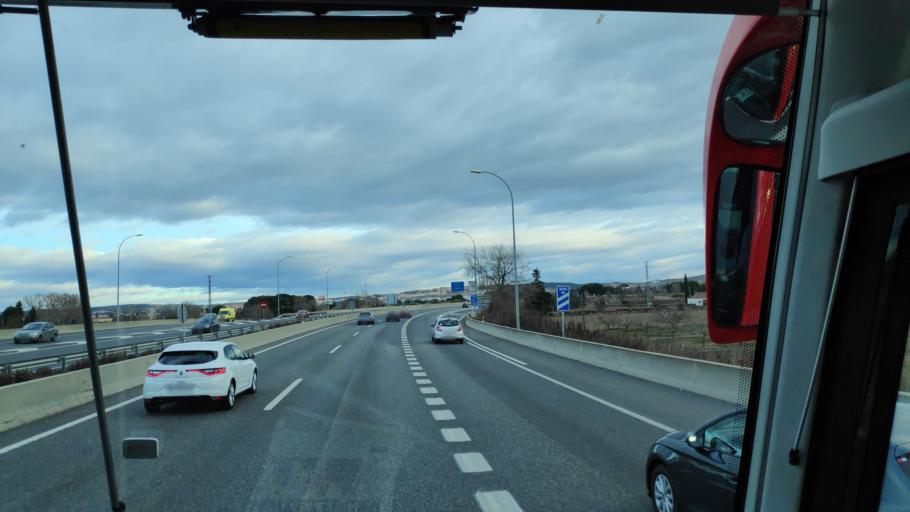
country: ES
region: Madrid
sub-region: Provincia de Madrid
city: Vaciamadrid
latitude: 40.3143
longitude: -3.4990
